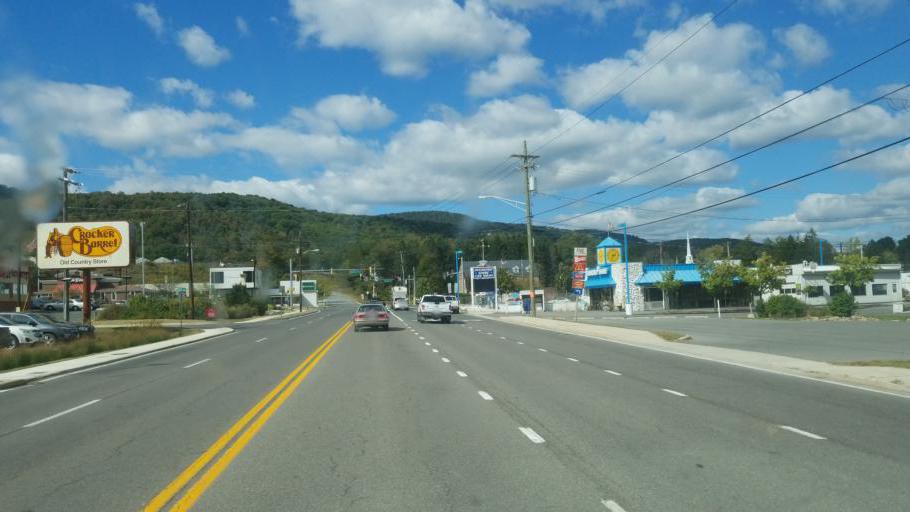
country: US
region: Maryland
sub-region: Allegany County
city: La Vale
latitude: 39.6378
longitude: -78.8299
